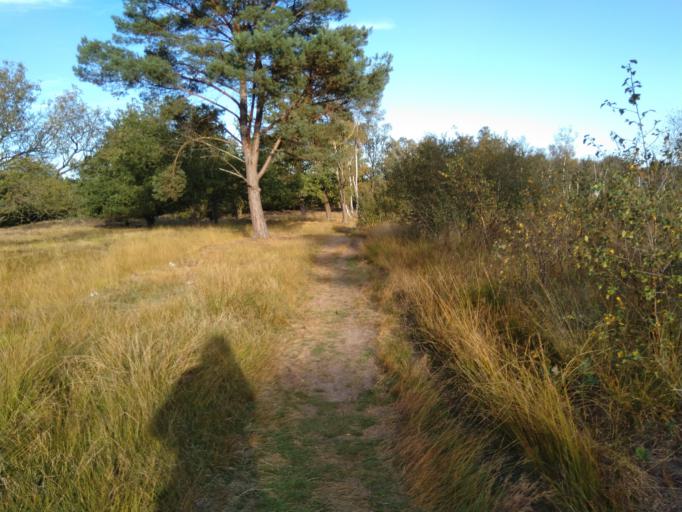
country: NL
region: Drenthe
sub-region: Gemeente Tynaarlo
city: Zuidlaren
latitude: 53.0709
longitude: 6.6533
